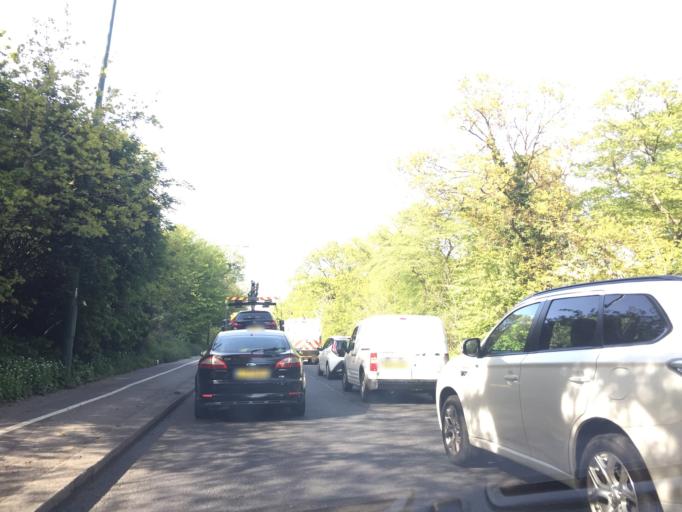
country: GB
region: England
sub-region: Greater London
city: Woodford Green
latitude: 51.5906
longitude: 0.0082
